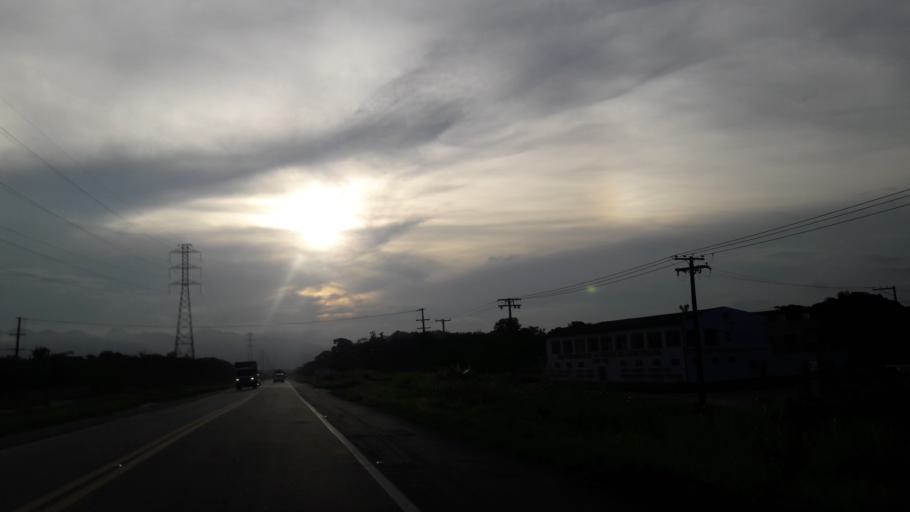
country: BR
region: Sao Paulo
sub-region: Peruibe
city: Peruibe
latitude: -24.2795
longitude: -46.9889
